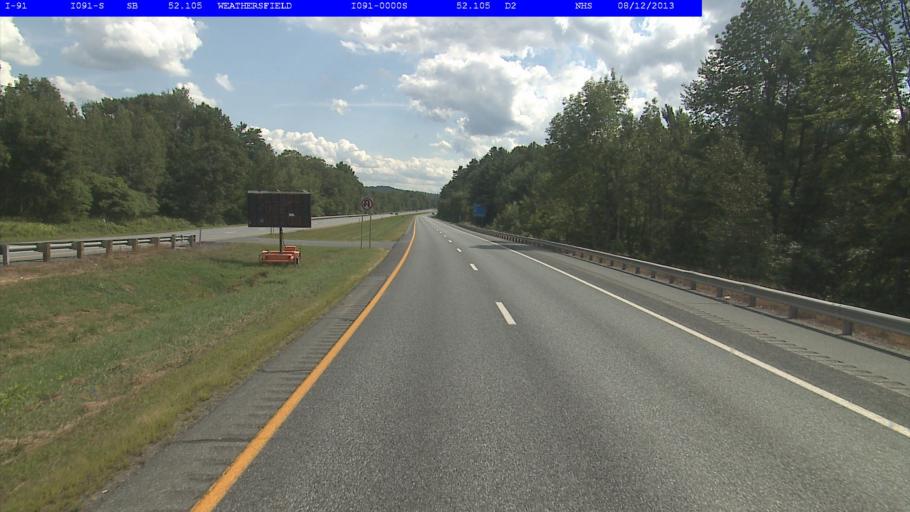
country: US
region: Vermont
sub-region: Windsor County
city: Windsor
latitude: 43.4132
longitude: -72.4155
